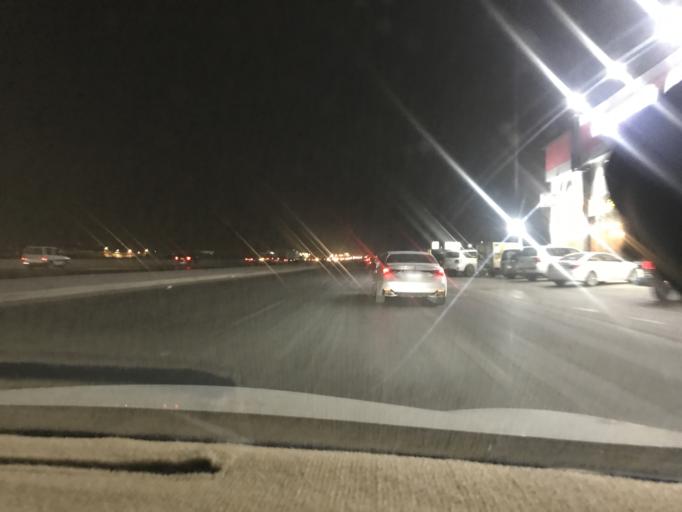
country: SA
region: Ar Riyad
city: Riyadh
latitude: 24.8484
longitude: 46.6035
